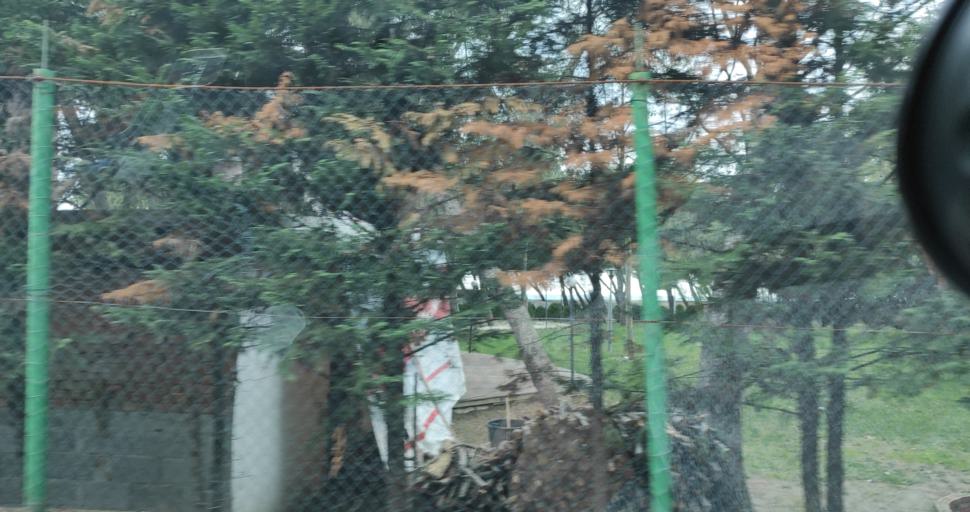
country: AL
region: Lezhe
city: Shengjin
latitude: 41.8189
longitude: 19.5652
